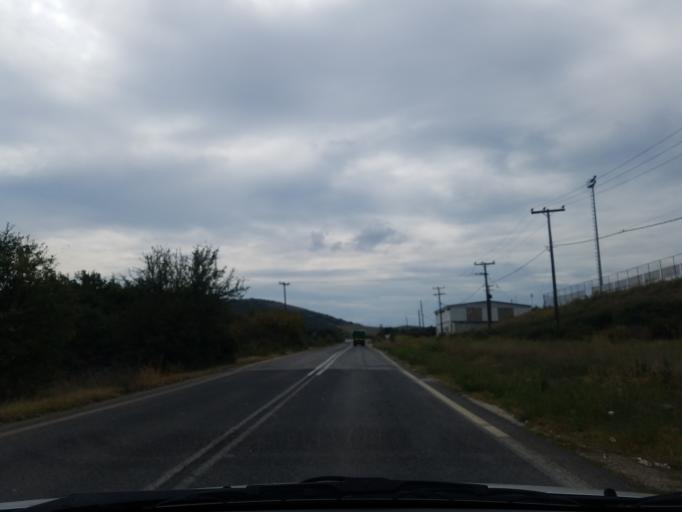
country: GR
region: Central Greece
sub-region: Nomos Fthiotidos
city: Domokos
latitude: 39.1168
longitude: 22.3105
